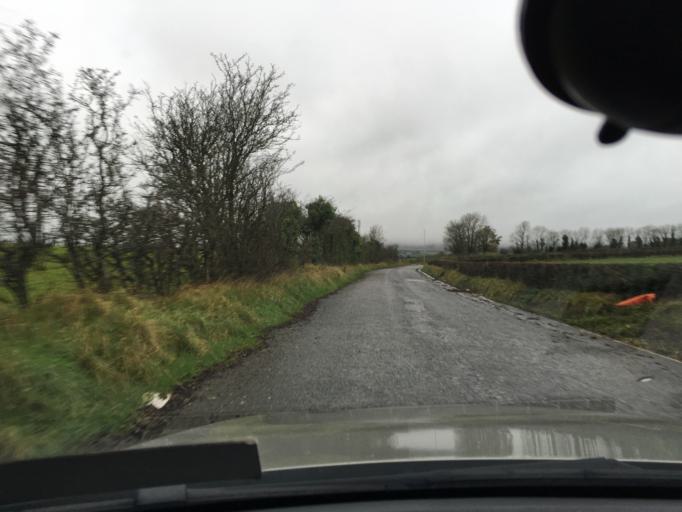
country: GB
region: Northern Ireland
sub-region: Larne District
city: Larne
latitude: 54.8338
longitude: -5.8719
